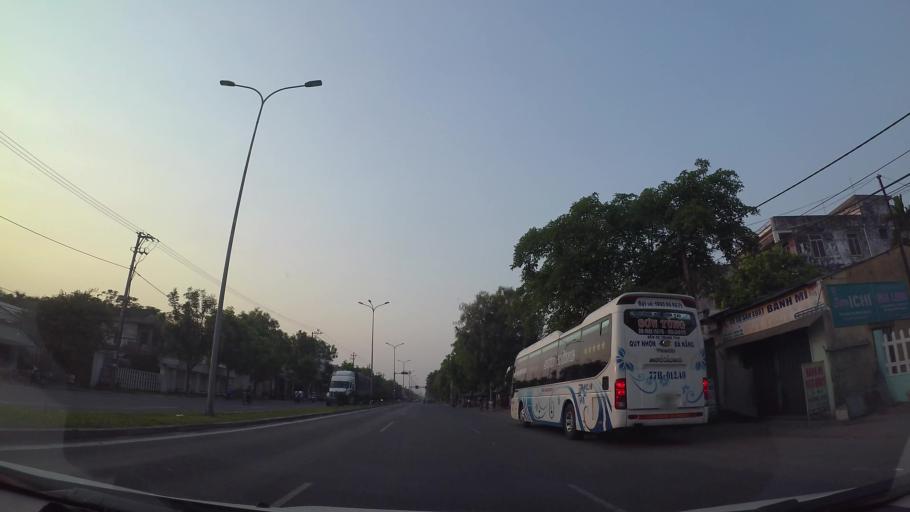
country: VN
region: Quang Nam
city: Quang Nam
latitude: 15.9487
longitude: 108.2198
